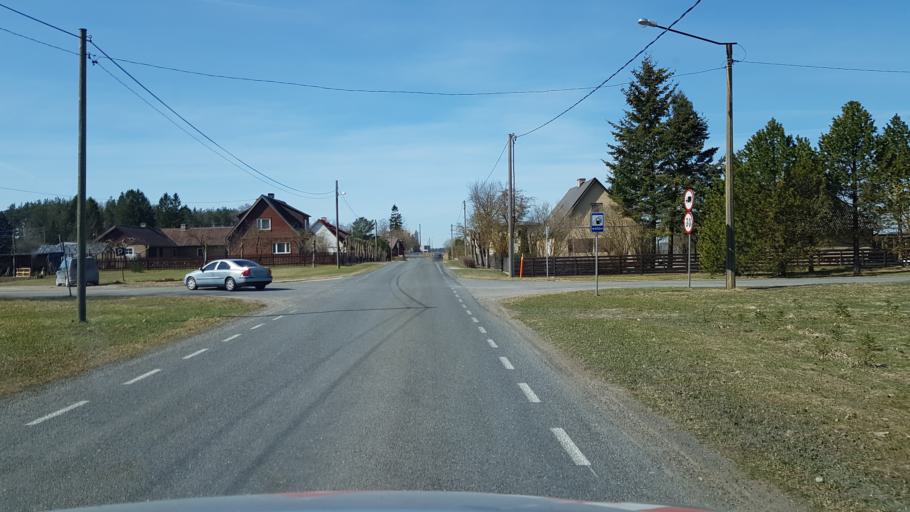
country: EE
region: Laeaene-Virumaa
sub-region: Vinni vald
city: Vinni
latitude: 59.2843
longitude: 26.4084
